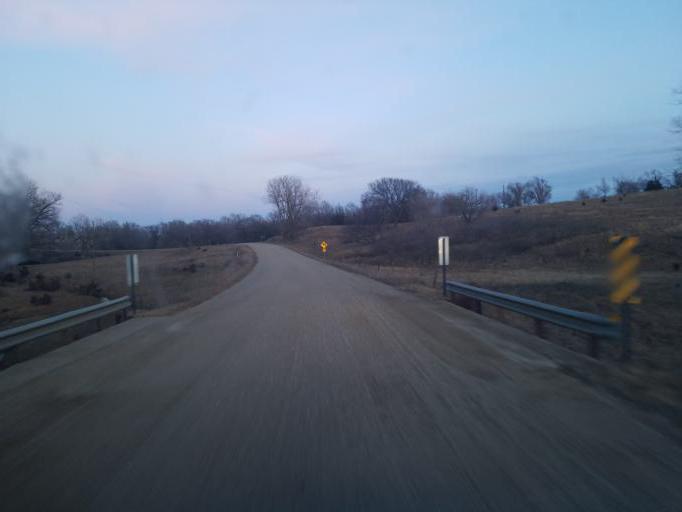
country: US
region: Nebraska
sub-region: Knox County
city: Center
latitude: 42.6165
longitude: -97.8405
